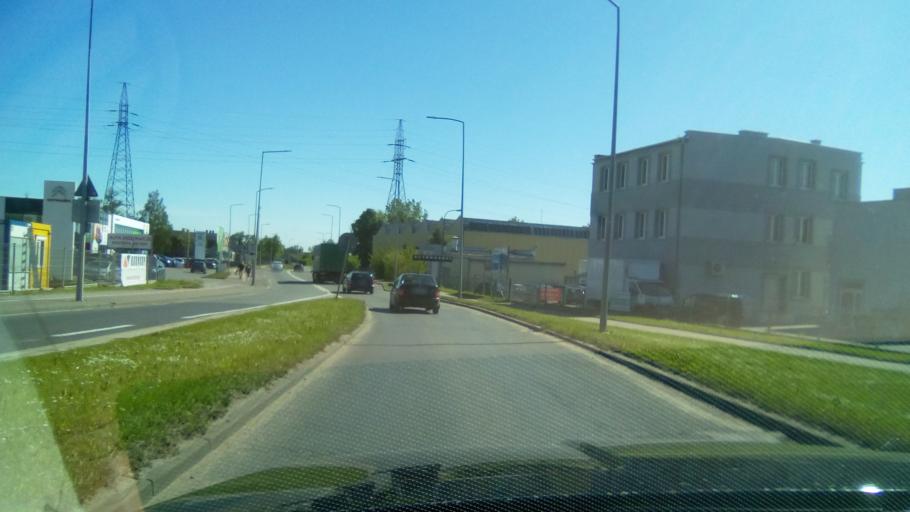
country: PL
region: Warmian-Masurian Voivodeship
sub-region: Powiat elblaski
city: Elblag
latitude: 54.1530
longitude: 19.3911
